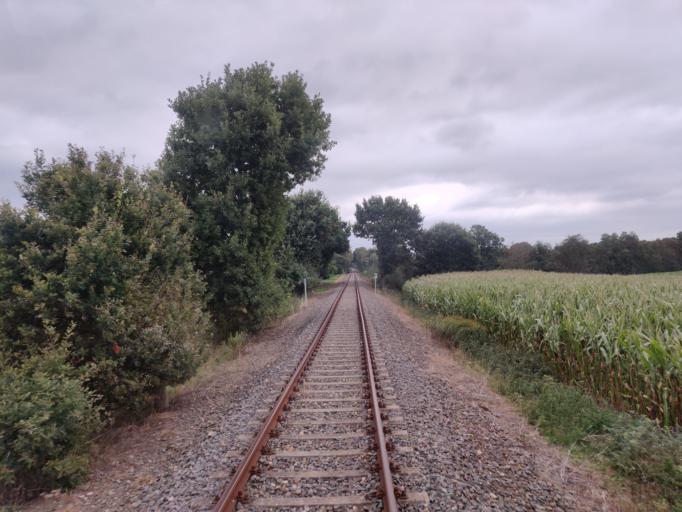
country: DE
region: Lower Saxony
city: Gnarrenburg
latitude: 53.3842
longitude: 9.0093
